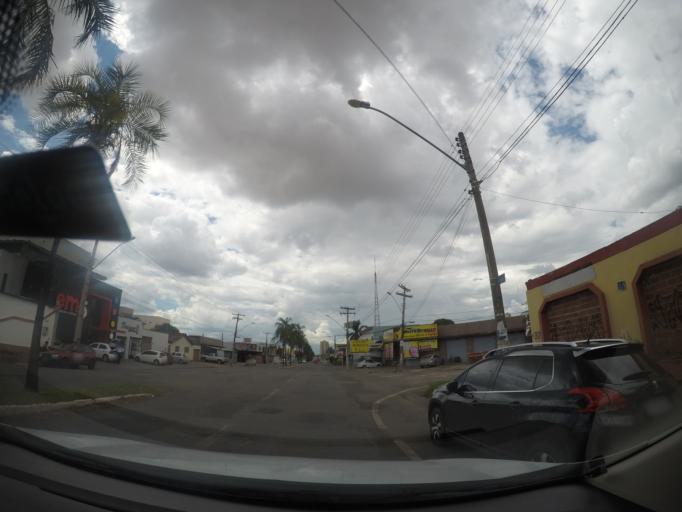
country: BR
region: Goias
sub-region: Goiania
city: Goiania
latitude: -16.6998
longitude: -49.2851
